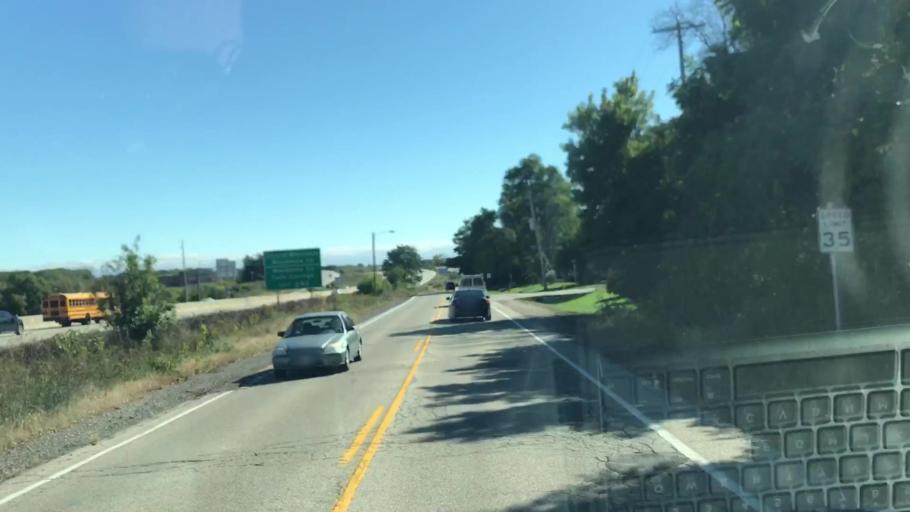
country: US
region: Wisconsin
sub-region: Waukesha County
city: Pewaukee
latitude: 43.0468
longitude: -88.2760
